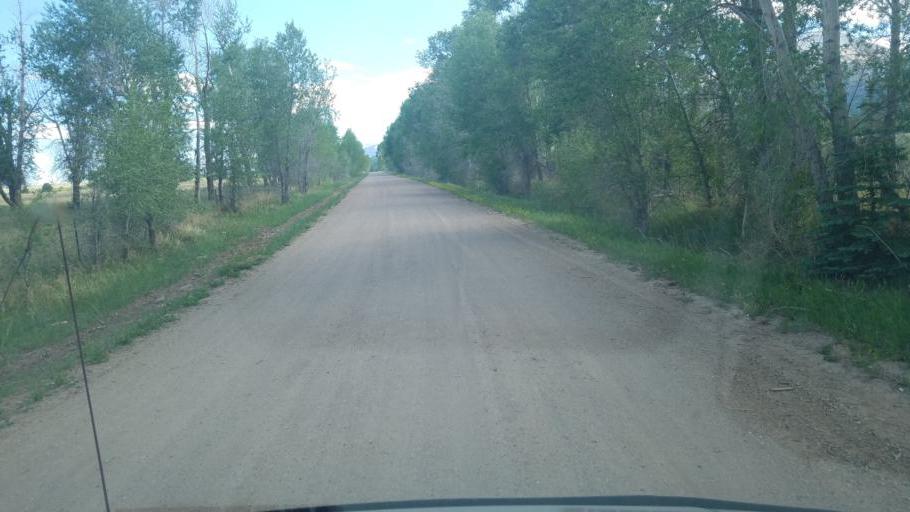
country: US
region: Colorado
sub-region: Custer County
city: Westcliffe
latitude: 38.2362
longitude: -105.5988
